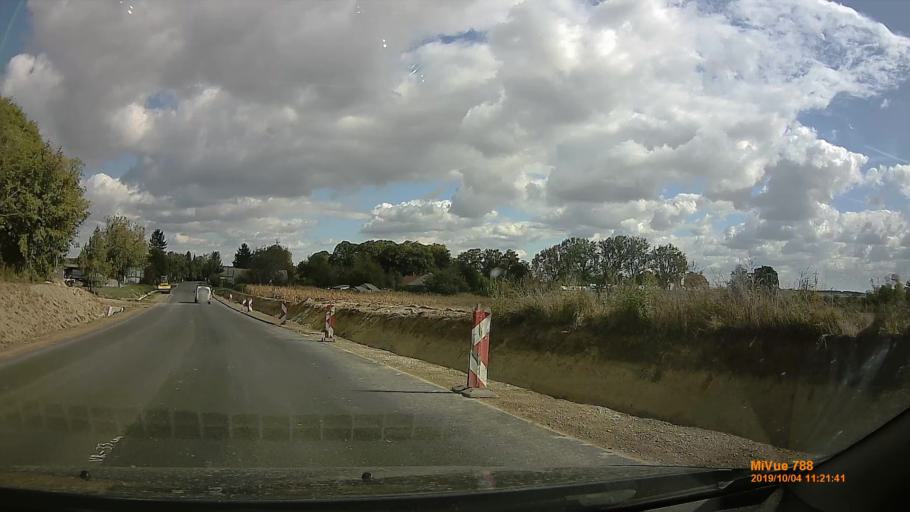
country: HU
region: Somogy
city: Kaposvar
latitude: 46.5014
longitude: 17.8126
